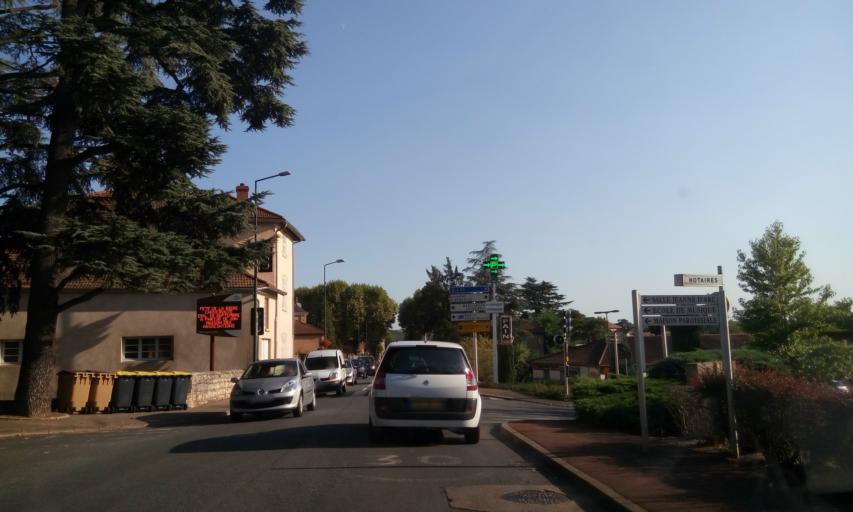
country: FR
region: Rhone-Alpes
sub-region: Departement du Rhone
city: Morance
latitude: 45.8771
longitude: 4.7104
